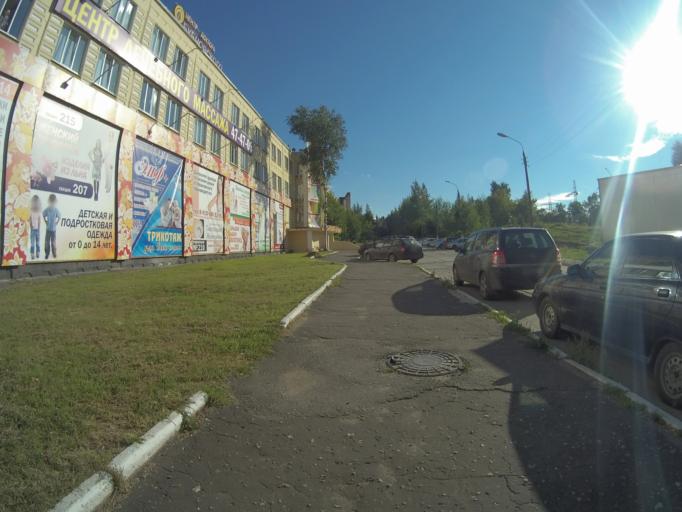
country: RU
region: Vladimir
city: Vladimir
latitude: 56.1642
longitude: 40.3848
